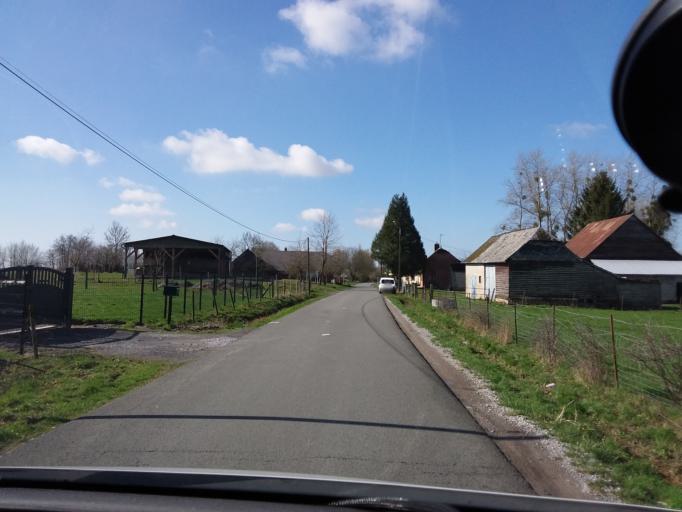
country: FR
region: Picardie
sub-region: Departement de l'Aisne
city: Origny-en-Thierache
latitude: 49.8406
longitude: 4.0677
